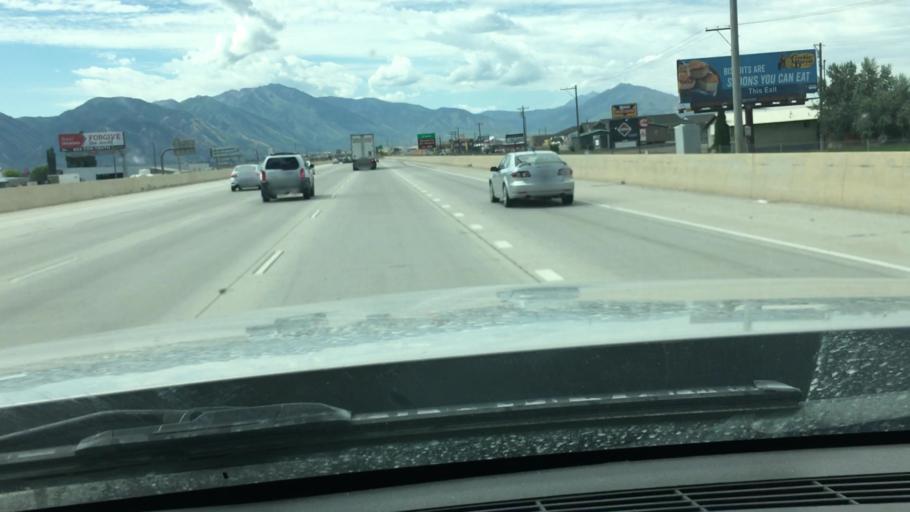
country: US
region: Utah
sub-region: Utah County
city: Springville
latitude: 40.1713
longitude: -111.6472
